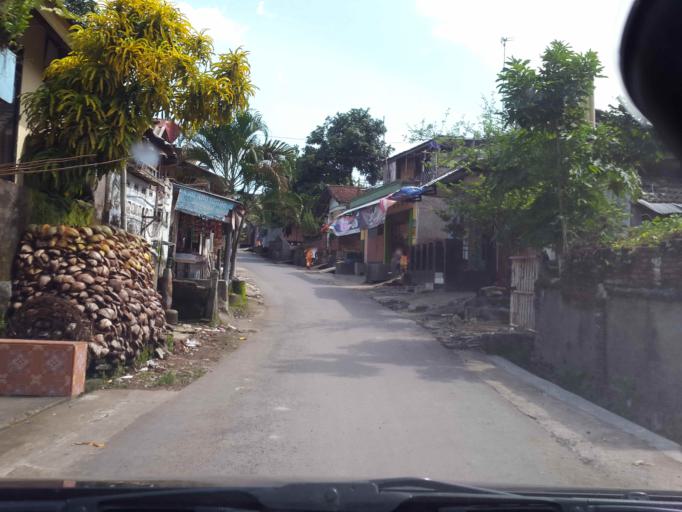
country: ID
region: West Nusa Tenggara
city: Jejelok
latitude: -8.6042
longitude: 116.1795
